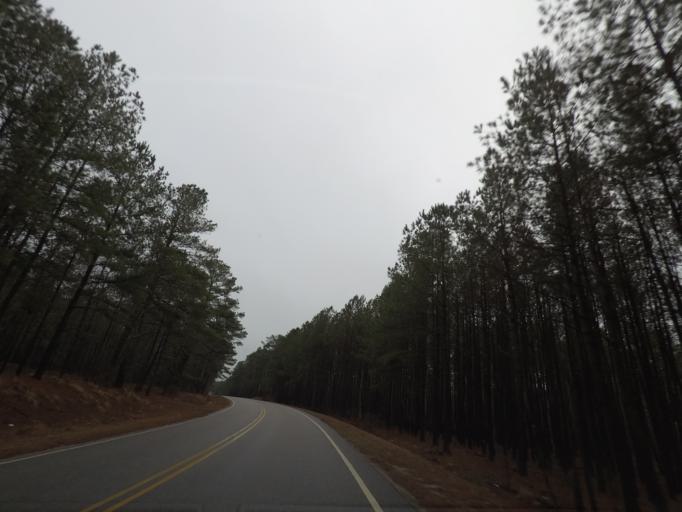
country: US
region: North Carolina
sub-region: Cumberland County
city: Spring Lake
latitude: 35.2665
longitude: -78.9951
